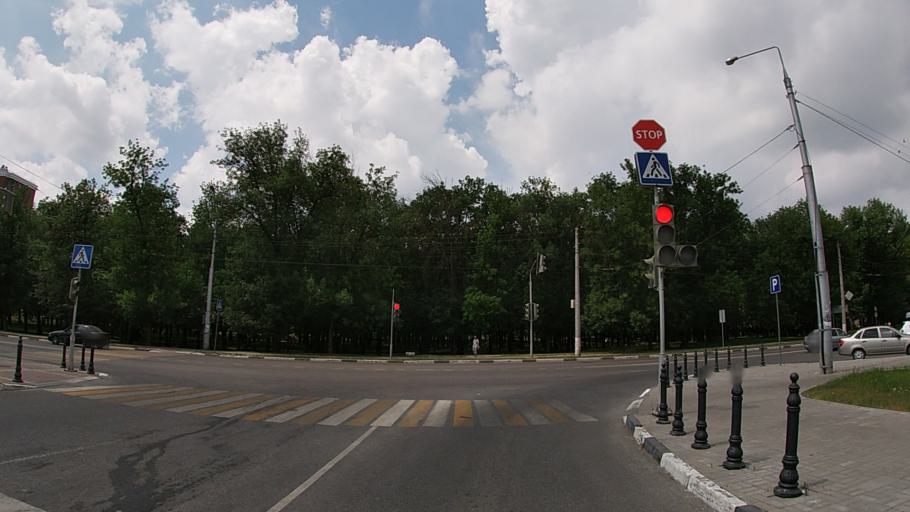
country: RU
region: Belgorod
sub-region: Belgorodskiy Rayon
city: Belgorod
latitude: 50.6071
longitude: 36.5916
